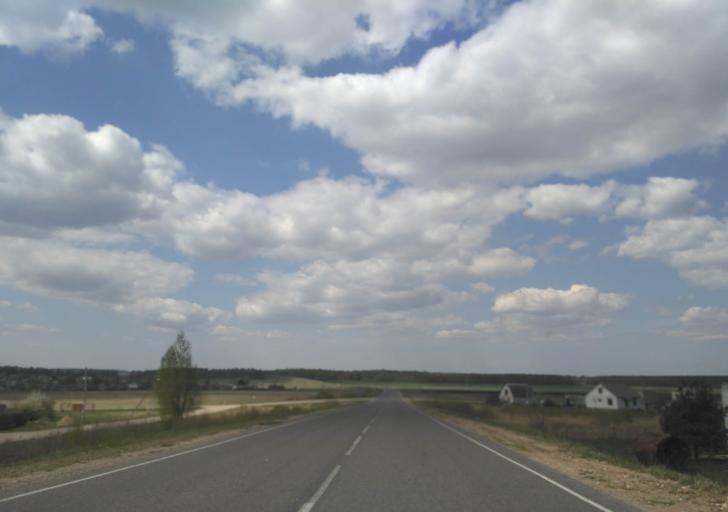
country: BY
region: Minsk
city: Vilyeyka
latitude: 54.5182
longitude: 26.9779
